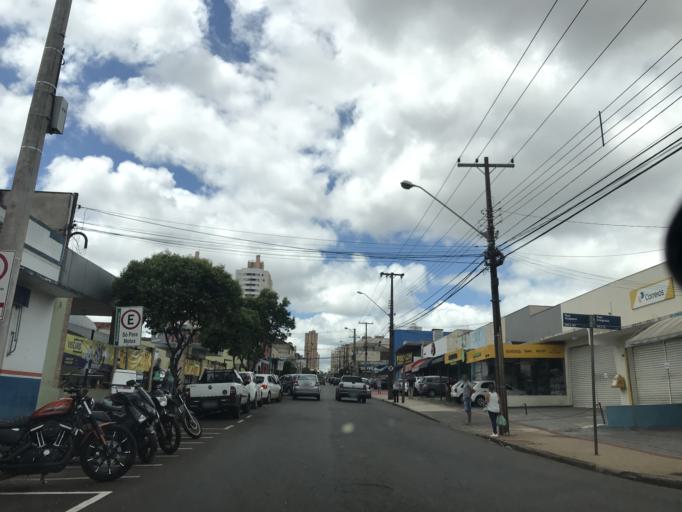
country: BR
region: Parana
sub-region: Londrina
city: Londrina
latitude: -23.3002
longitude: -51.1628
